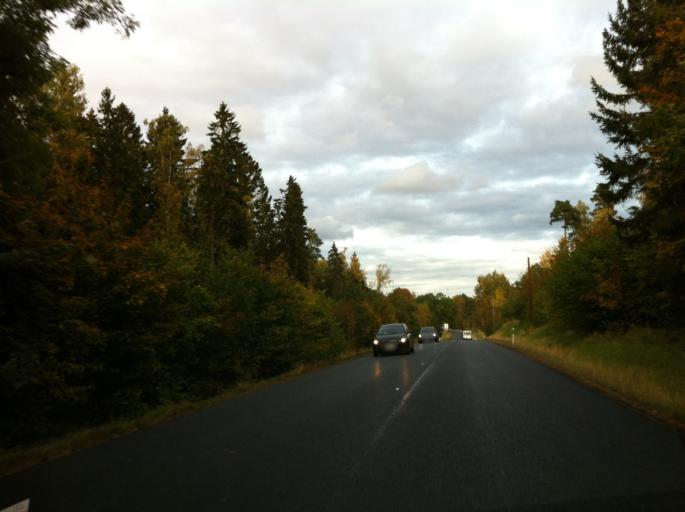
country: SE
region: OEstergoetland
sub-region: Motala Kommun
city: Ryd
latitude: 58.7104
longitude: 14.9649
